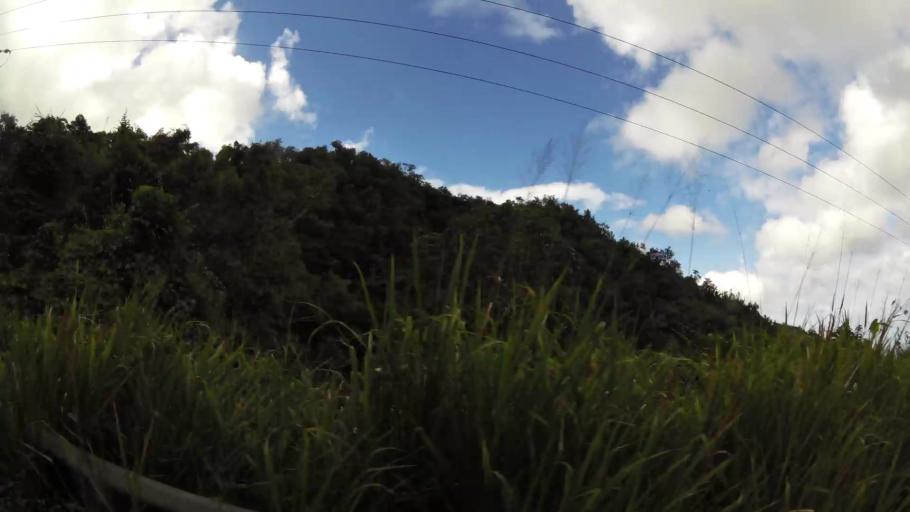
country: MQ
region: Martinique
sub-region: Martinique
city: Les Trois-Ilets
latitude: 14.5151
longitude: -61.0743
